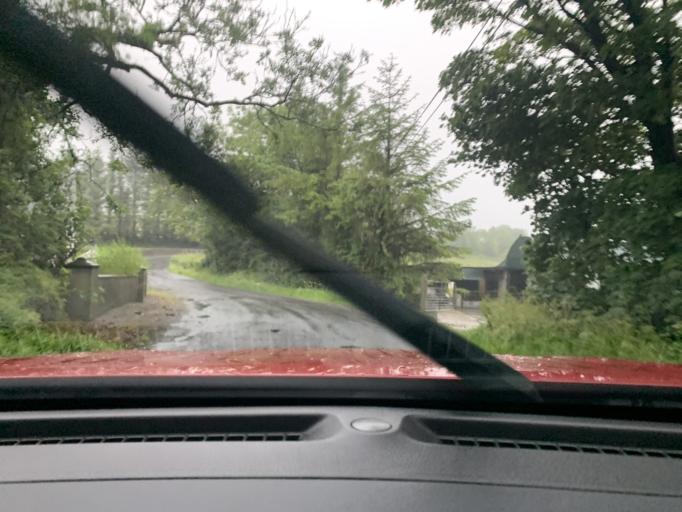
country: IE
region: Connaught
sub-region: Sligo
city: Sligo
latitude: 54.3286
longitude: -8.4208
